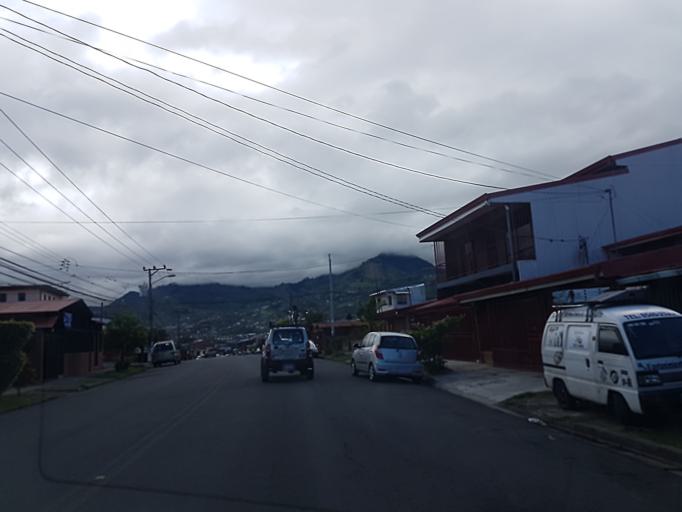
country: CR
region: San Jose
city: San Felipe
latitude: 9.9191
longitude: -84.1007
